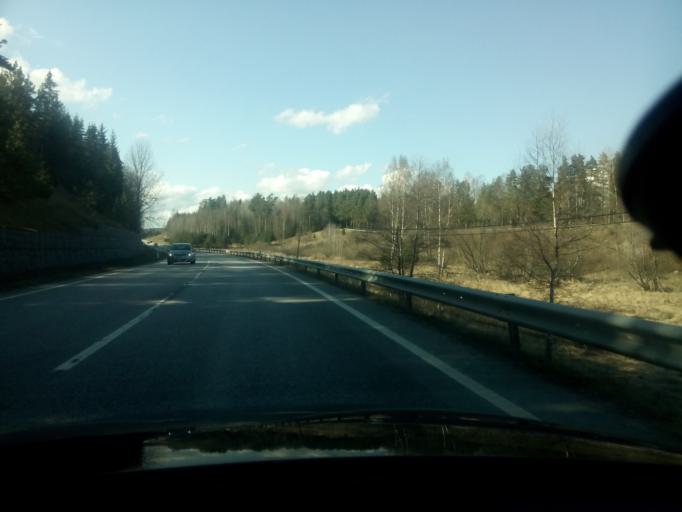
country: SE
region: Soedermanland
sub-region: Flens Kommun
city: Malmkoping
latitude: 59.1158
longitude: 16.7611
